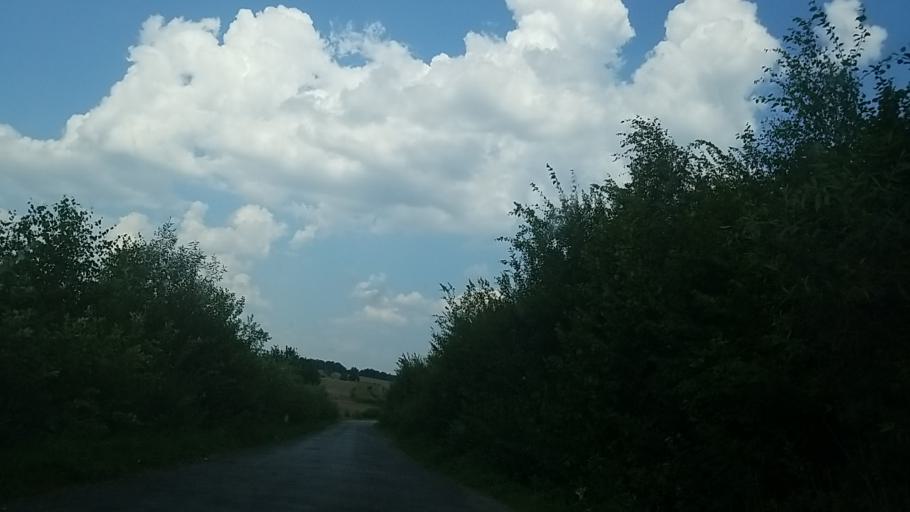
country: PL
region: Lublin Voivodeship
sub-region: Powiat bilgorajski
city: Goraj
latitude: 50.7229
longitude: 22.6205
